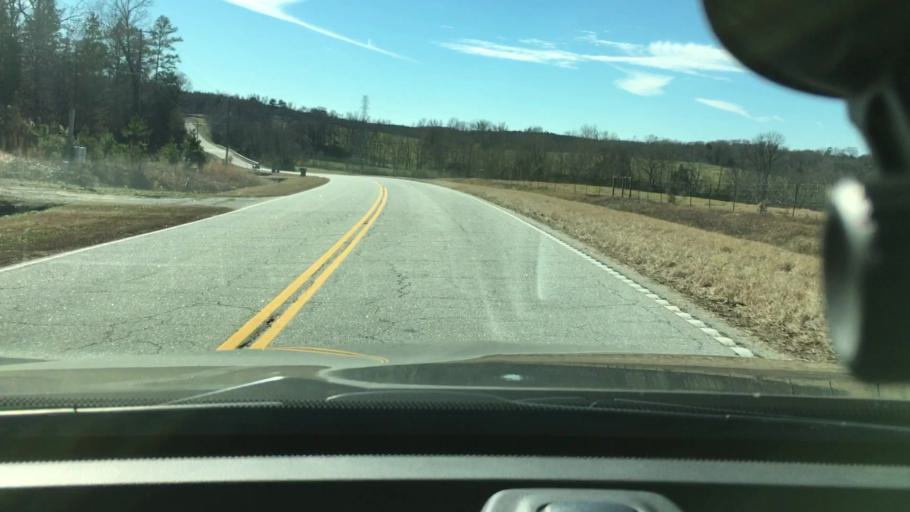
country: US
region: South Carolina
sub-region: Cherokee County
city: Gaffney
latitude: 35.0272
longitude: -81.6871
